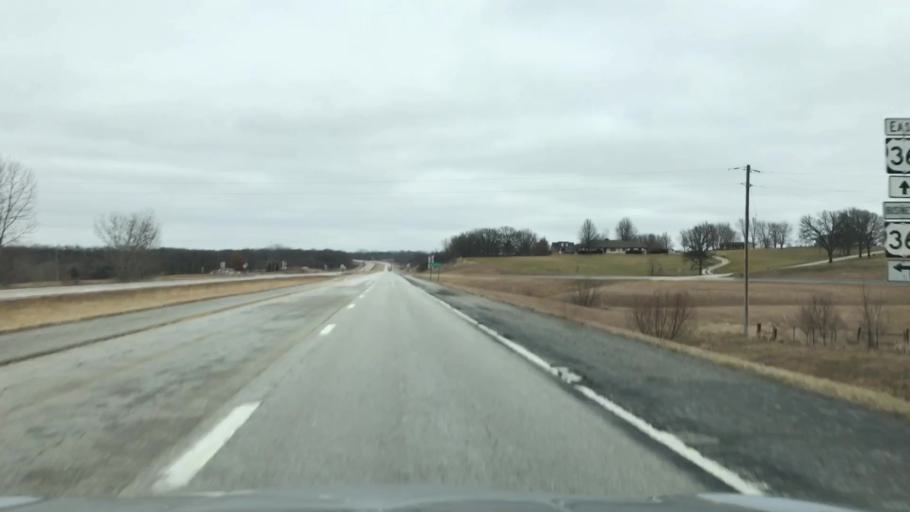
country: US
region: Missouri
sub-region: Caldwell County
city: Hamilton
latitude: 39.7428
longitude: -94.0403
